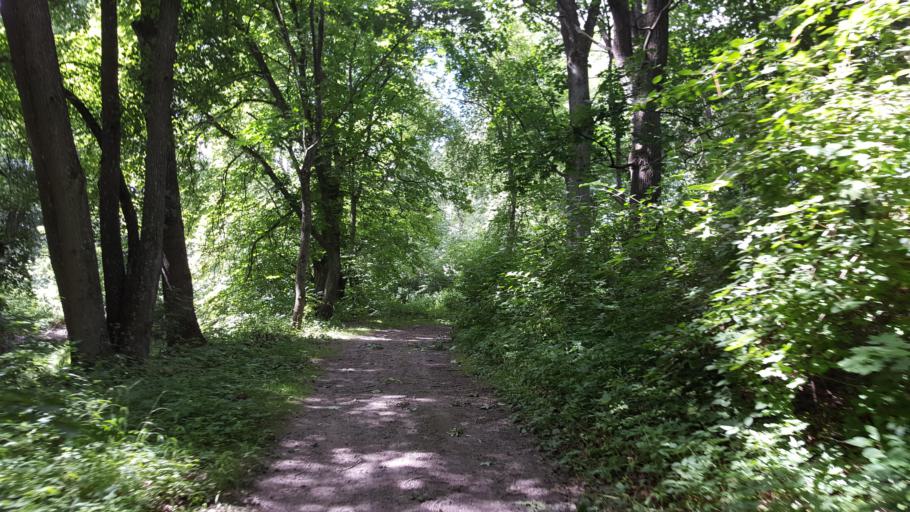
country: BY
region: Brest
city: Kamyanyets
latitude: 52.3155
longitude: 23.9269
